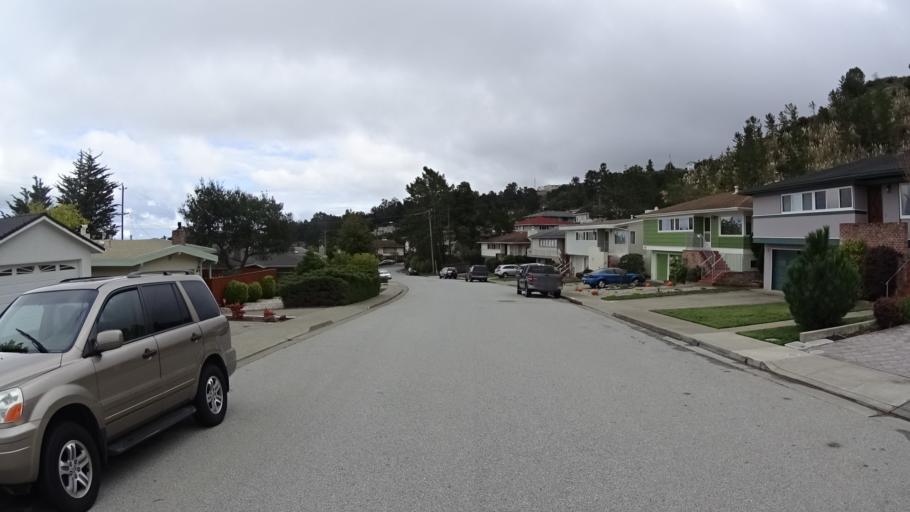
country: US
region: California
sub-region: San Mateo County
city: San Bruno
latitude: 37.6005
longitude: -122.4187
